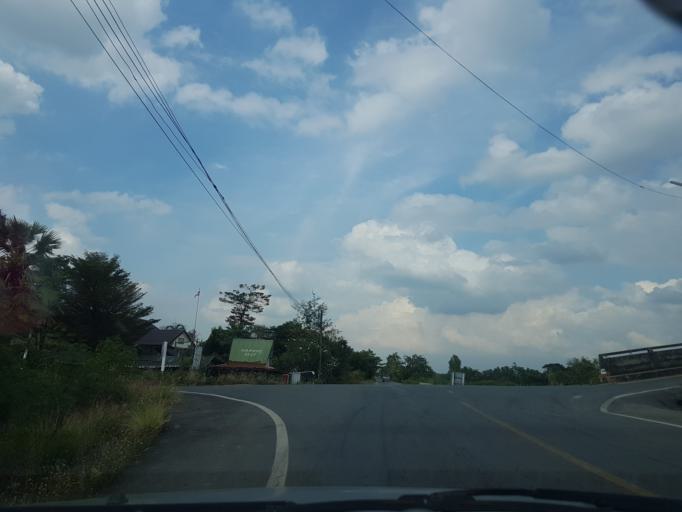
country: TH
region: Pathum Thani
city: Nong Suea
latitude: 14.1964
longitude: 100.8914
